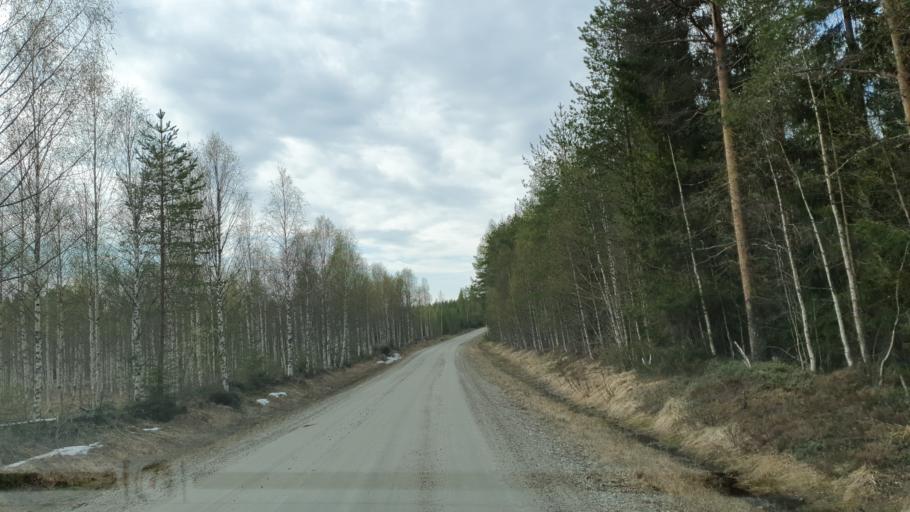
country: FI
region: Kainuu
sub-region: Kehys-Kainuu
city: Kuhmo
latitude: 64.0972
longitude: 29.9167
